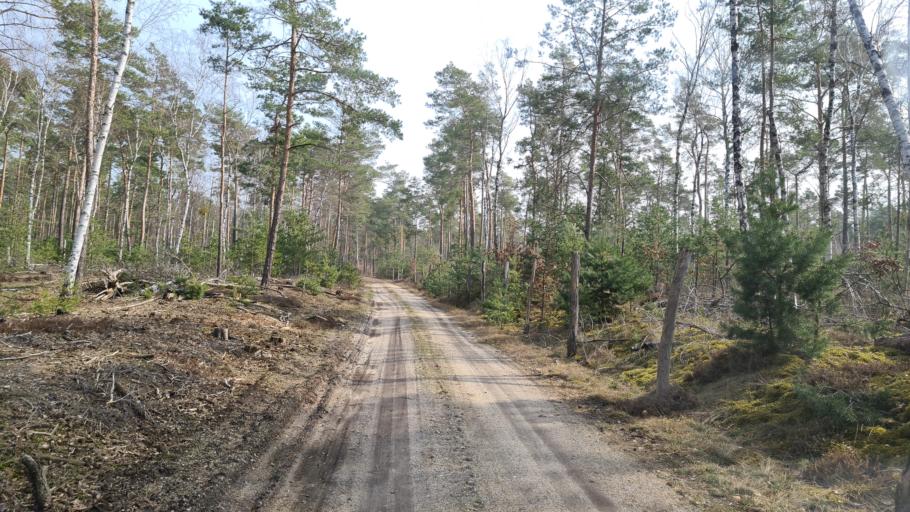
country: DE
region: Brandenburg
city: Trobitz
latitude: 51.6303
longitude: 13.4210
